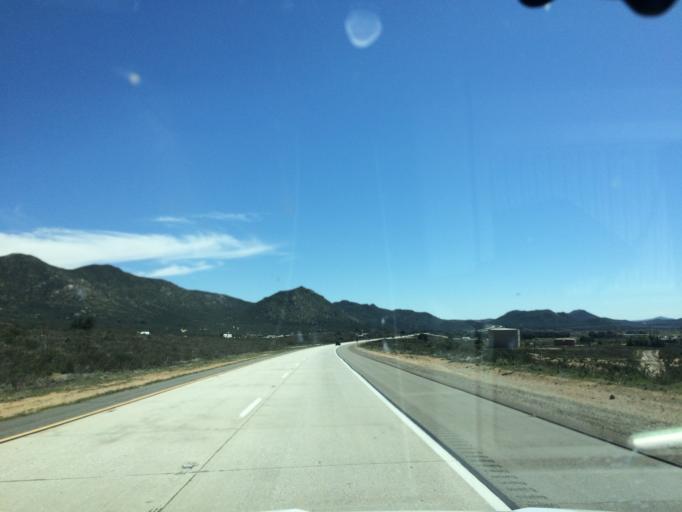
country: US
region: California
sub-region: San Diego County
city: Pine Valley
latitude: 32.7701
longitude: -116.4902
